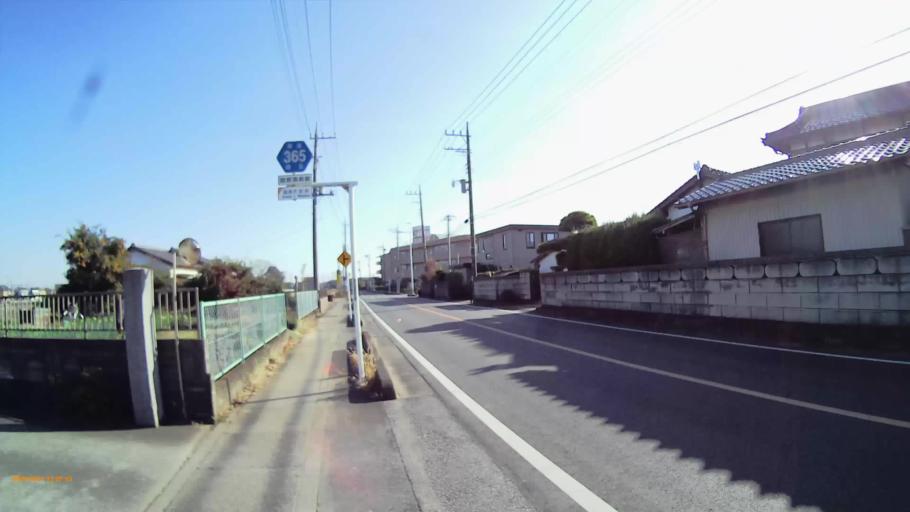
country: JP
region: Saitama
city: Fukiage-fujimi
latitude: 36.0904
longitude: 139.4674
